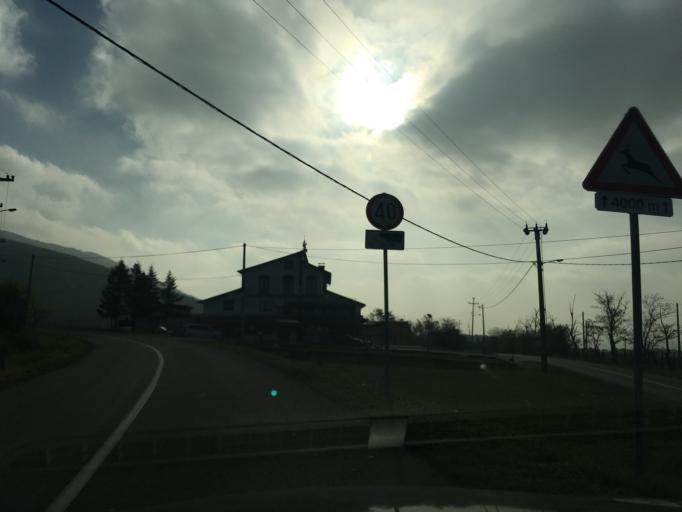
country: RS
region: Central Serbia
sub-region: Belgrade
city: Sopot
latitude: 44.4825
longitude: 20.5576
